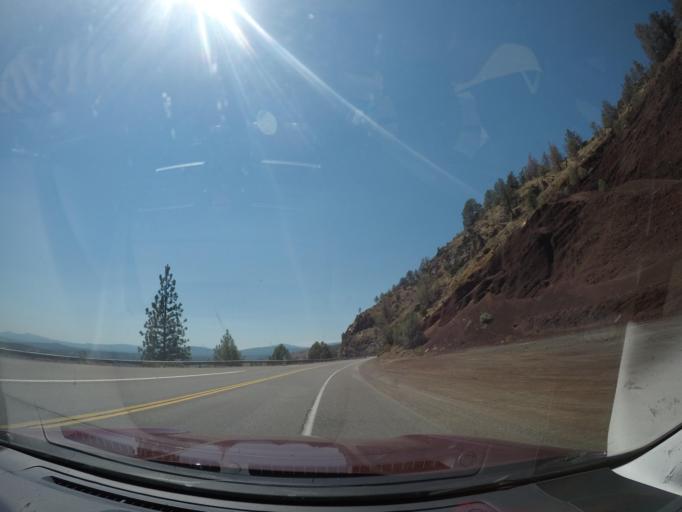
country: US
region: California
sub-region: Shasta County
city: Burney
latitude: 40.9928
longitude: -121.4837
